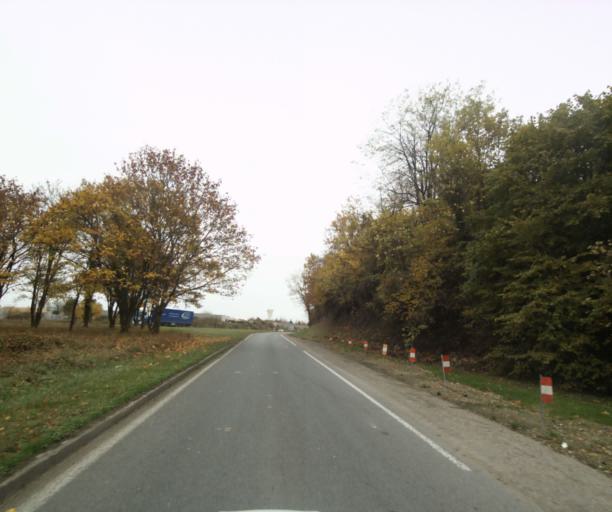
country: FR
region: Poitou-Charentes
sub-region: Departement de la Charente-Maritime
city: Saintes
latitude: 45.7398
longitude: -0.6613
